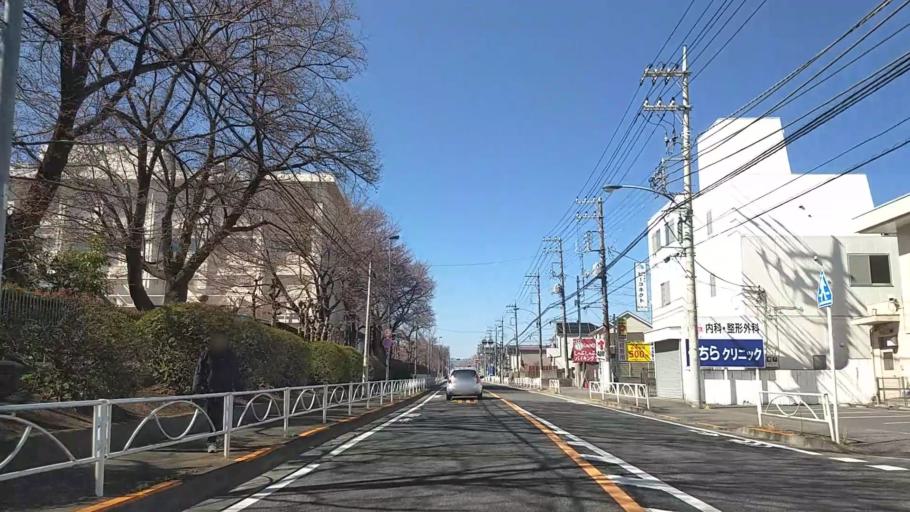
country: JP
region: Tokyo
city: Hino
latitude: 35.6702
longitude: 139.3742
